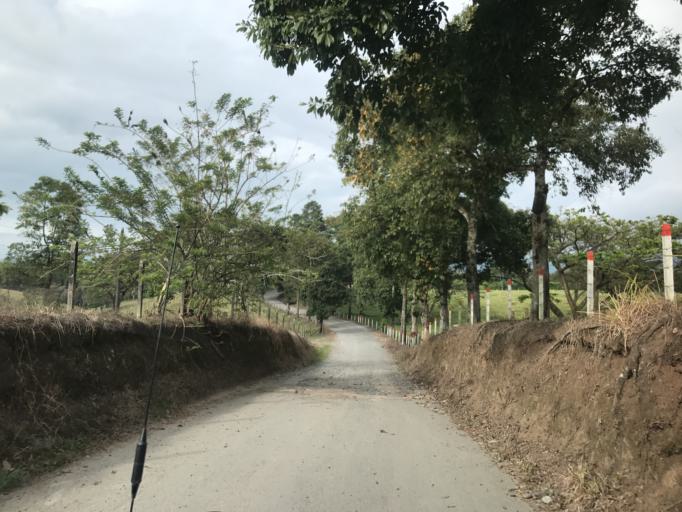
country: CO
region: Quindio
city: Montenegro
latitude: 4.5384
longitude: -75.8377
